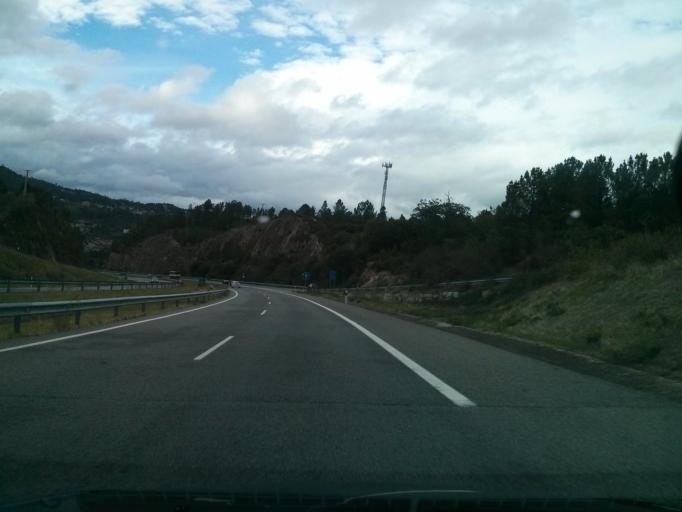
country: ES
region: Galicia
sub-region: Provincia de Ourense
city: Ourense
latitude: 42.3074
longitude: -7.8754
